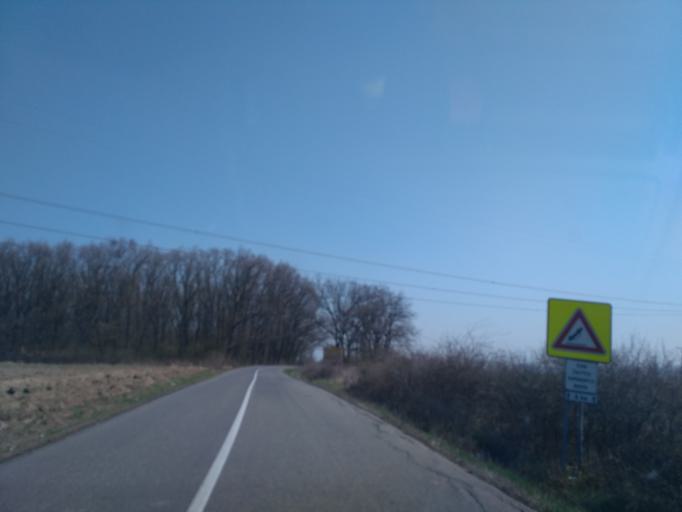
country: SK
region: Kosicky
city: Secovce
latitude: 48.7323
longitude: 21.5956
